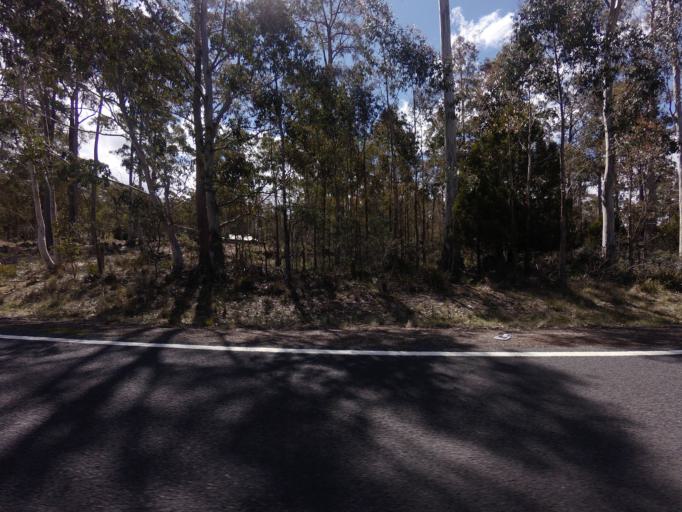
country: AU
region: Tasmania
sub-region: Northern Midlands
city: Evandale
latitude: -42.0326
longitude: 147.8228
